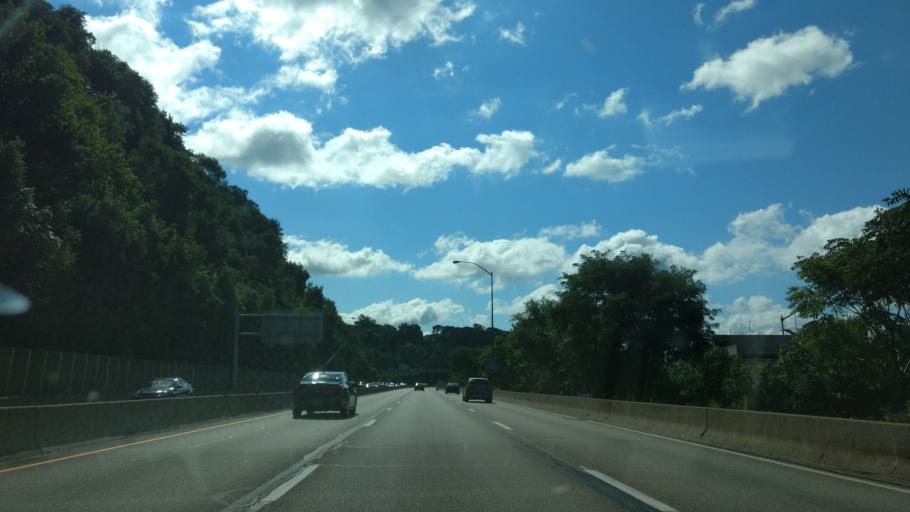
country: US
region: Pennsylvania
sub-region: Allegheny County
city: Bloomfield
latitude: 40.4334
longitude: -79.9629
